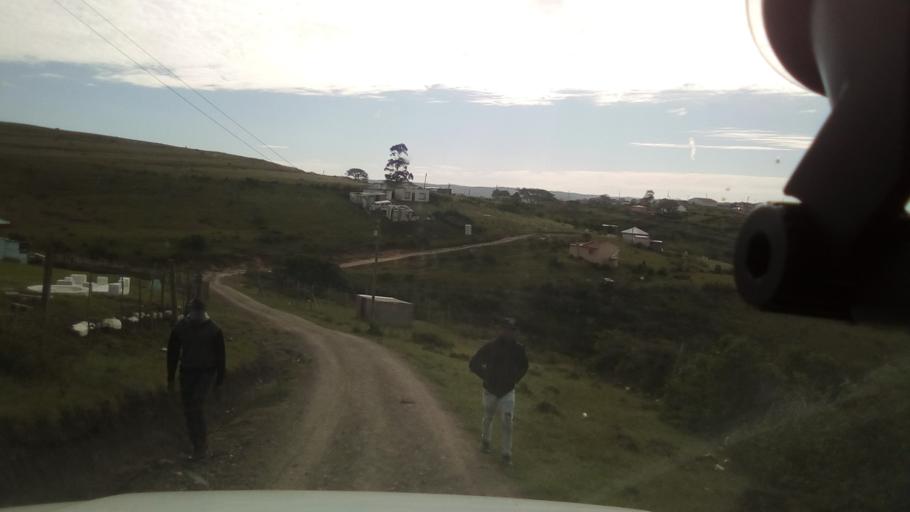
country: ZA
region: Eastern Cape
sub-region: Buffalo City Metropolitan Municipality
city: East London
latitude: -32.7976
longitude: 27.9561
